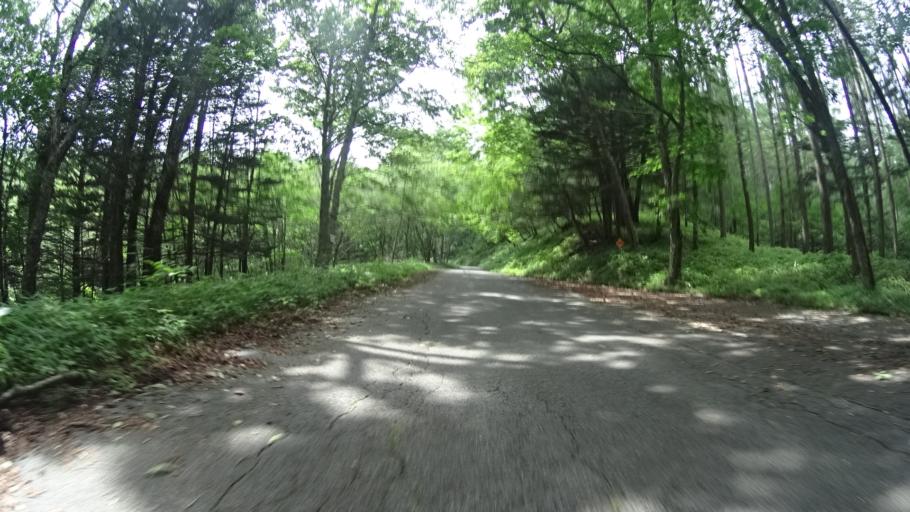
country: JP
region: Yamanashi
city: Enzan
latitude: 35.8033
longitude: 138.6337
